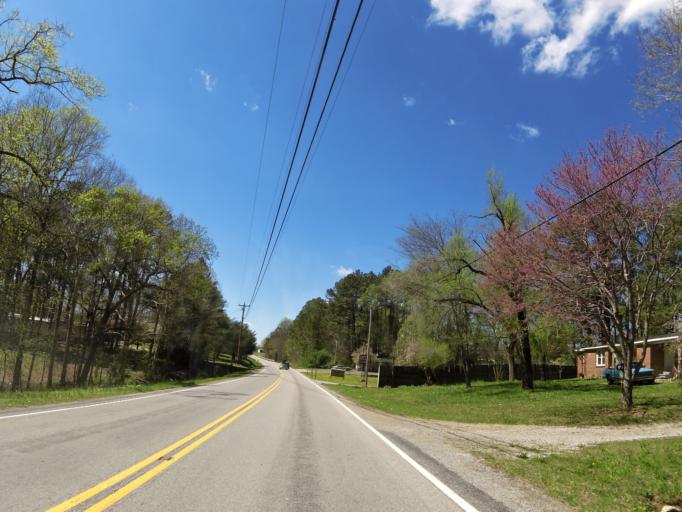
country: US
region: Tennessee
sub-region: DeKalb County
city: Smithville
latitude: 35.9518
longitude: -85.7516
